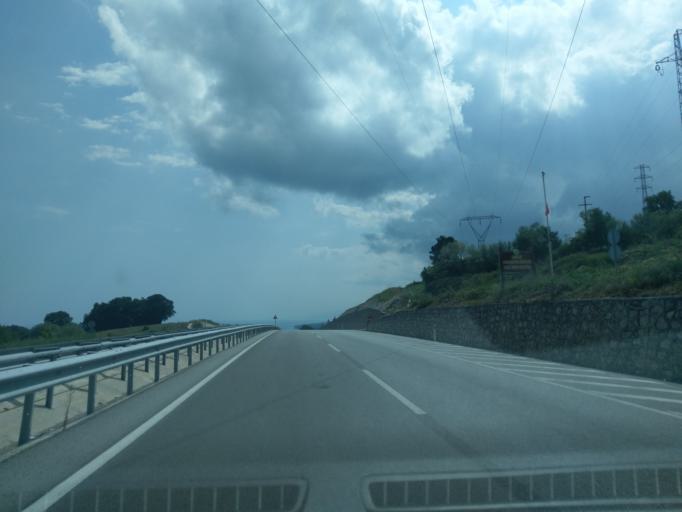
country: TR
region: Sinop
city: Kabali
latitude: 41.8525
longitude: 35.1185
